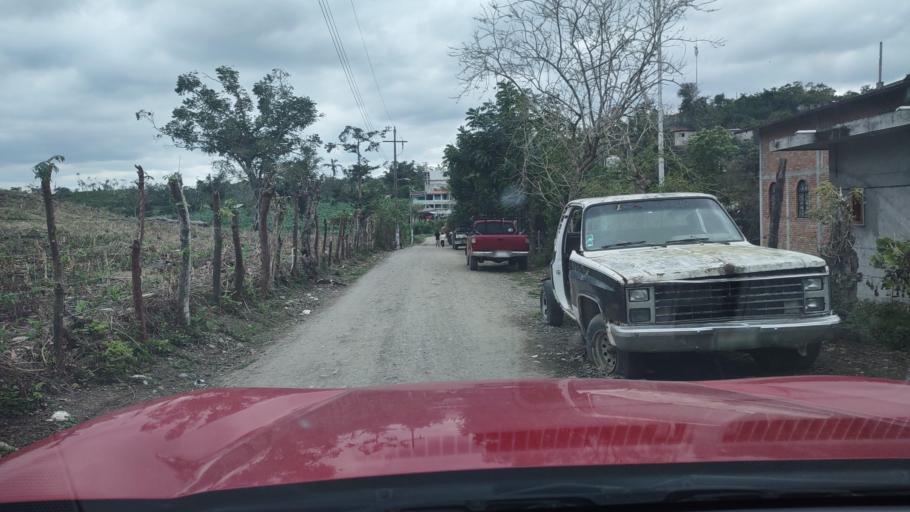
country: MX
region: Veracruz
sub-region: Papantla
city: Polutla
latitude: 20.4674
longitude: -97.2552
